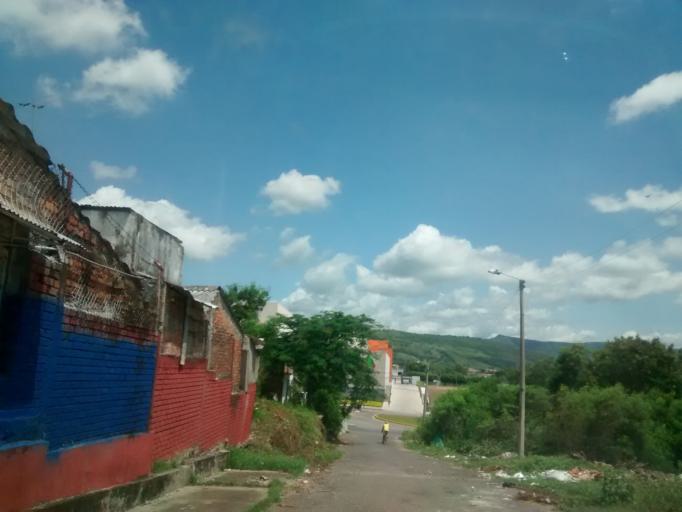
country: CO
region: Cundinamarca
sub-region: Girardot
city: Girardot City
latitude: 4.3067
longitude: -74.7958
